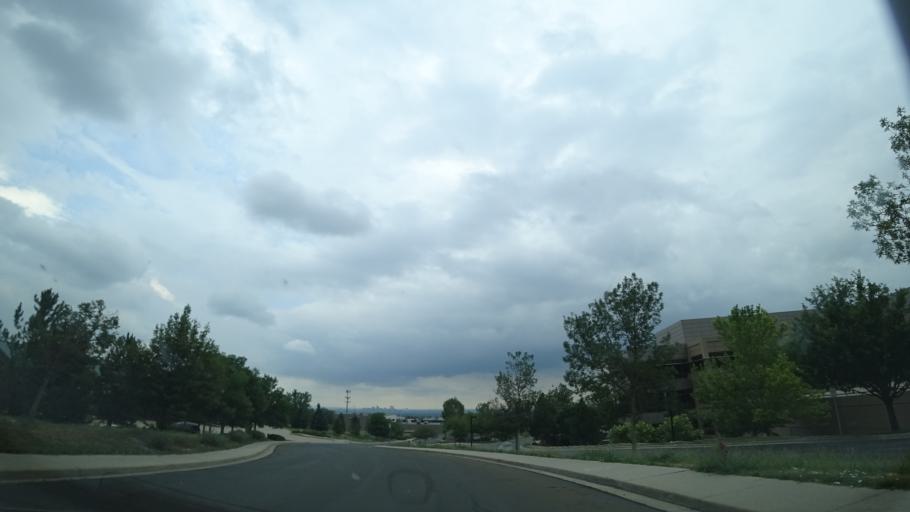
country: US
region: Colorado
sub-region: Jefferson County
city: West Pleasant View
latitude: 39.7098
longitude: -105.1400
